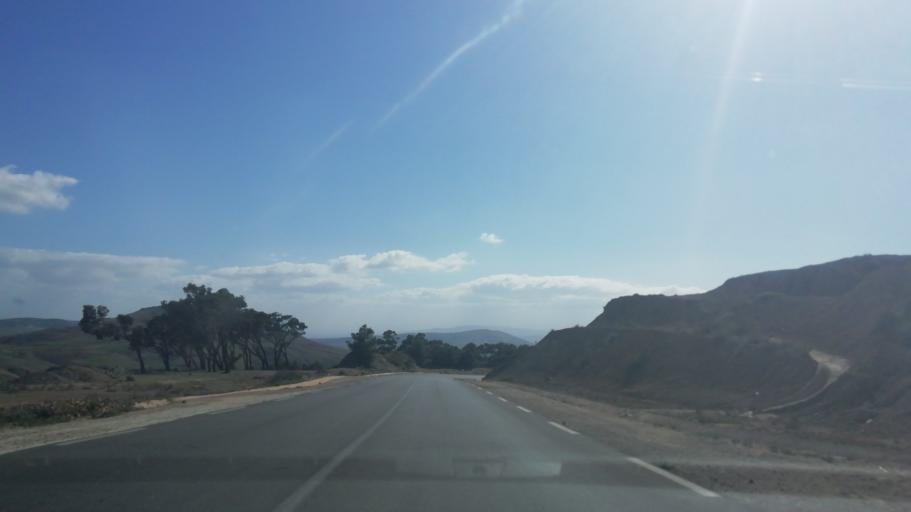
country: DZ
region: Relizane
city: Djidiouia
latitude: 36.0928
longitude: 0.5196
